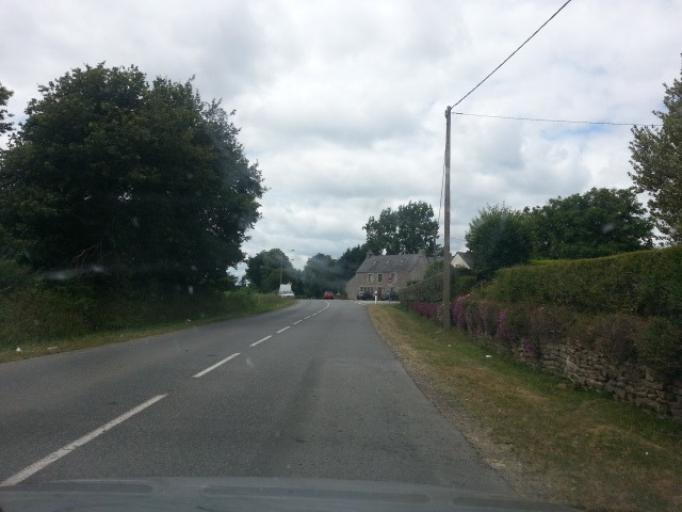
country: FR
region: Brittany
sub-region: Departement du Finistere
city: Melgven
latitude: 47.8857
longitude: -3.8192
